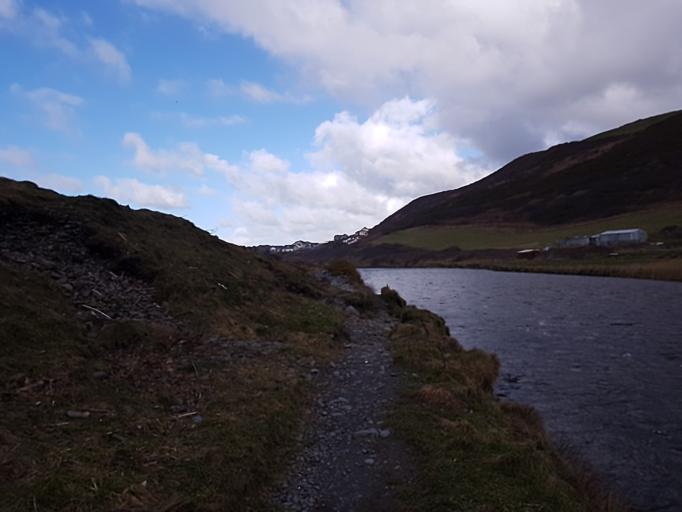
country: GB
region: Wales
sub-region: County of Ceredigion
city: Penparcau
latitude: 52.4008
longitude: -4.0880
